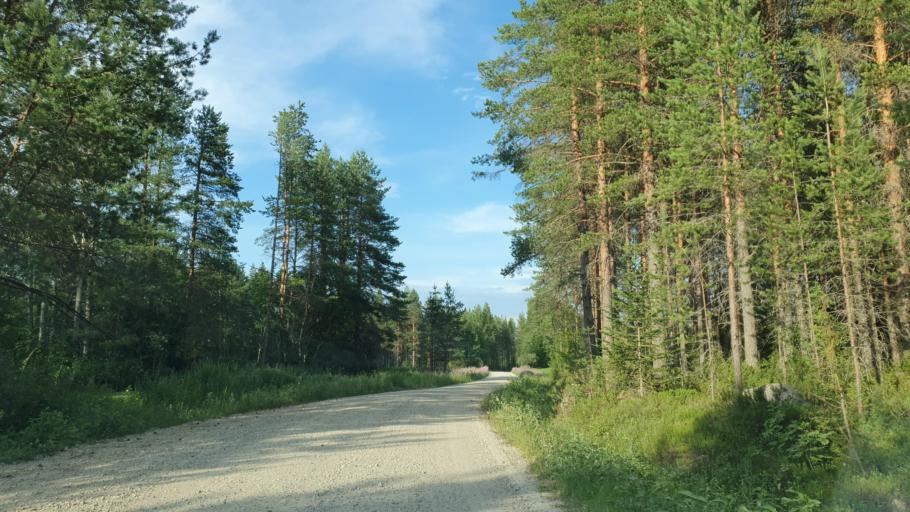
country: FI
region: Kainuu
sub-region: Kehys-Kainuu
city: Kuhmo
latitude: 64.3140
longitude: 29.5652
